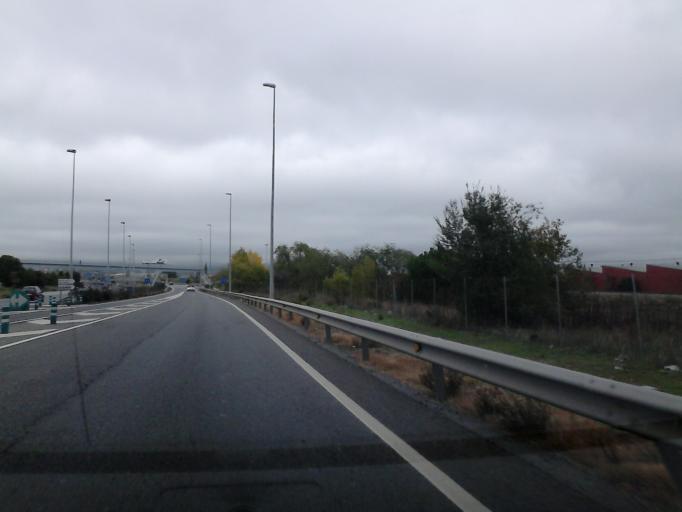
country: ES
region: Madrid
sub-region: Provincia de Madrid
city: Las Matas
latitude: 40.5290
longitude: -3.8866
